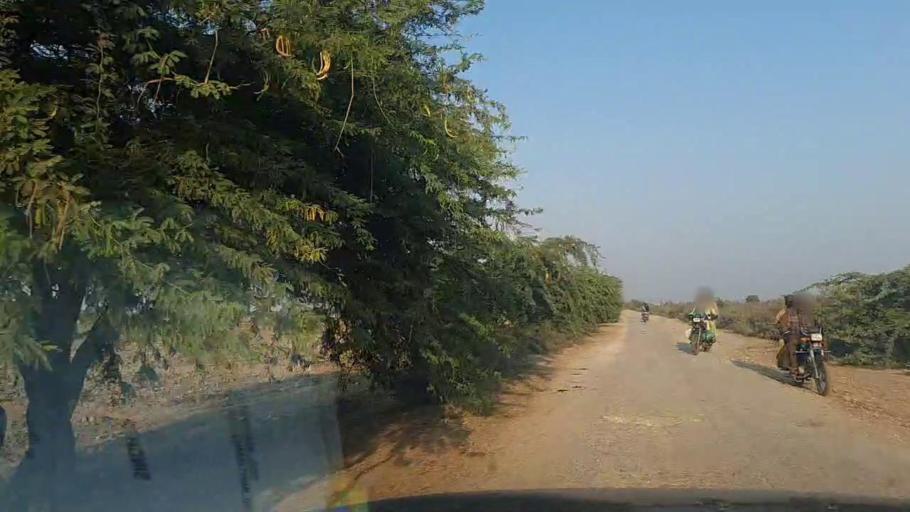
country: PK
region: Sindh
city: Keti Bandar
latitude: 24.2702
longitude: 67.5761
